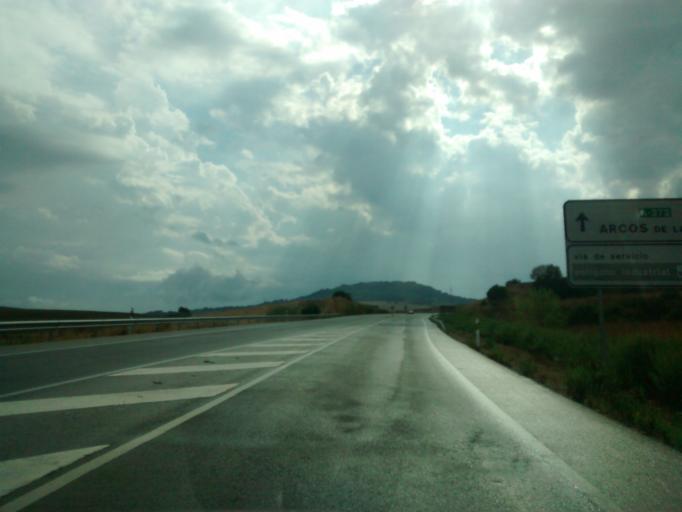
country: ES
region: Andalusia
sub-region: Provincia de Cadiz
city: El Bosque
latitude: 36.7526
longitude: -5.5244
